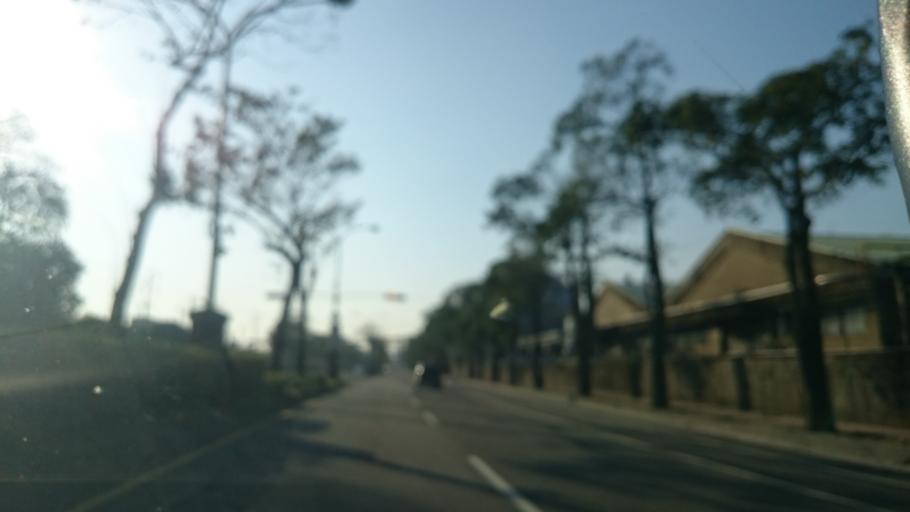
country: TW
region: Taiwan
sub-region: Miaoli
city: Miaoli
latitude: 24.6827
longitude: 120.8930
